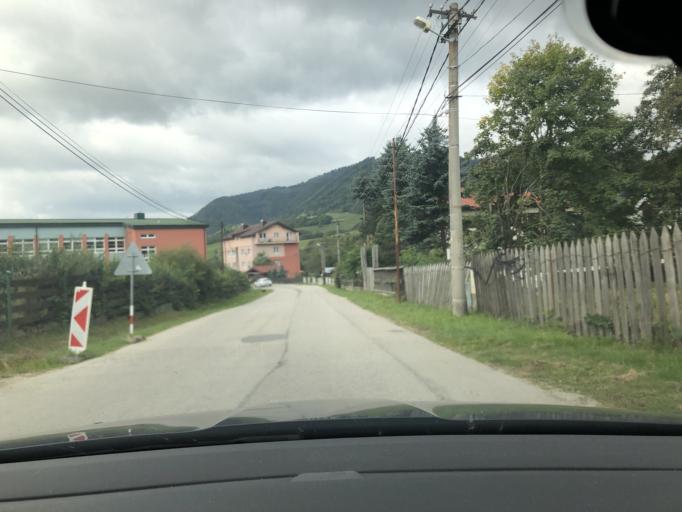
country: SK
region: Zilinsky
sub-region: Okres Zilina
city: Terchova
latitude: 49.2786
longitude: 19.0471
